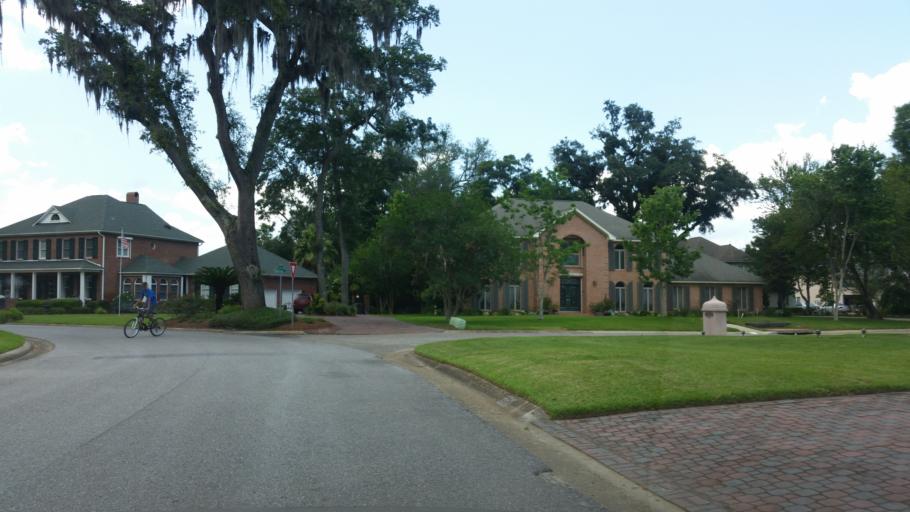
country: US
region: Florida
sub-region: Escambia County
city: Ferry Pass
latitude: 30.5180
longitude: -87.1726
